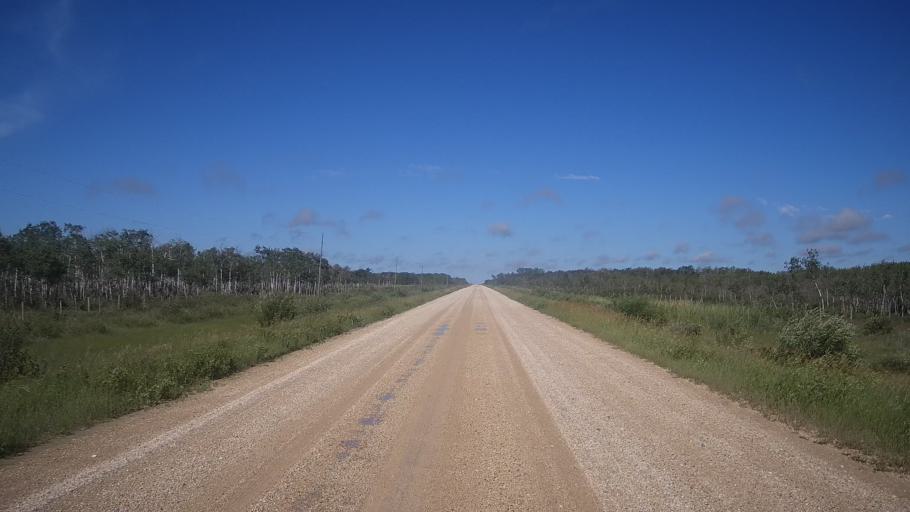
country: CA
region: Manitoba
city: Stonewall
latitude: 50.2411
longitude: -97.7521
